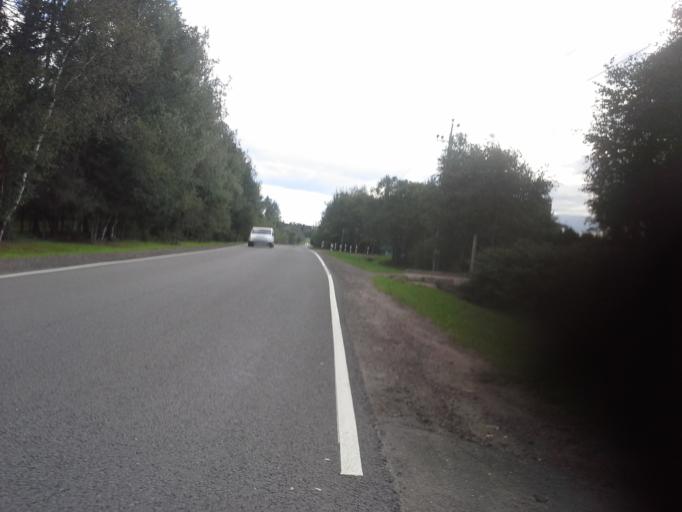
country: RU
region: Moskovskaya
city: Kievskij
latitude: 55.4840
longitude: 36.9100
